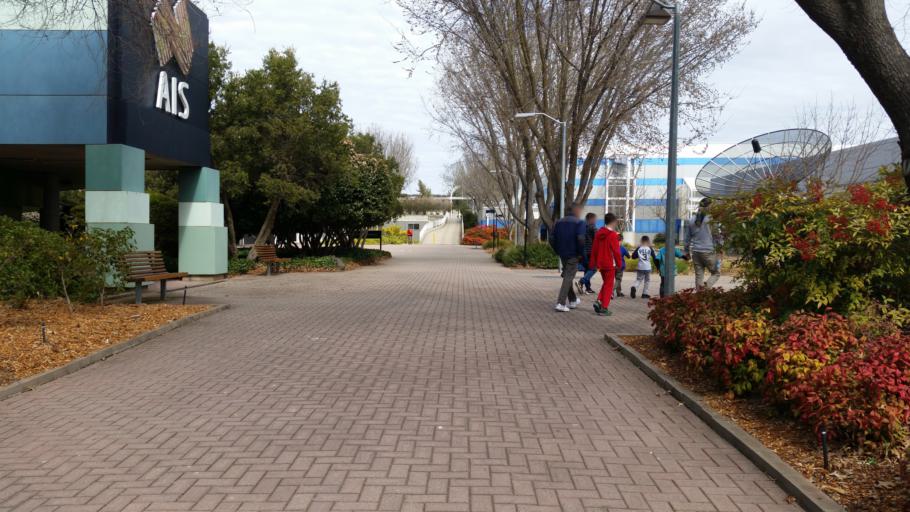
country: AU
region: Australian Capital Territory
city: Kaleen
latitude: -35.2459
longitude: 149.1034
